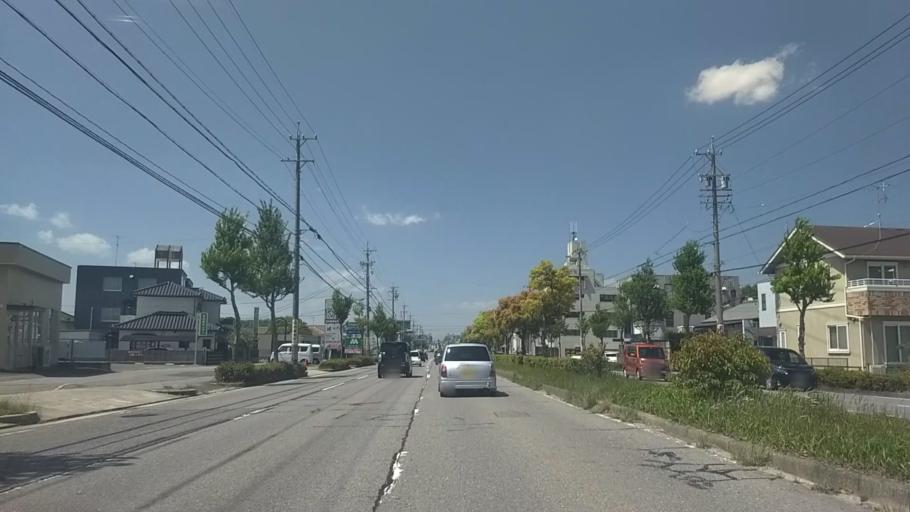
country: JP
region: Aichi
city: Okazaki
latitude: 34.9643
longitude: 137.1841
